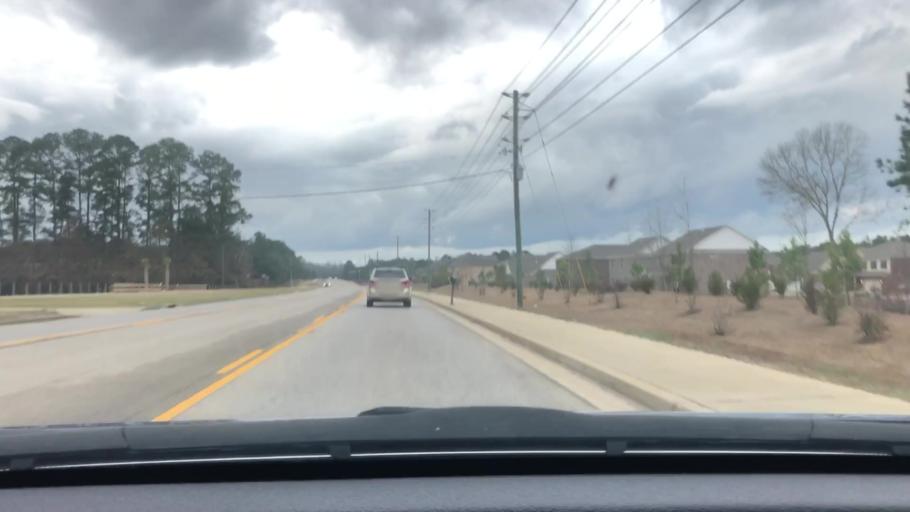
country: US
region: South Carolina
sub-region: Sumter County
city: Cane Savannah
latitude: 33.9291
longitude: -80.4104
